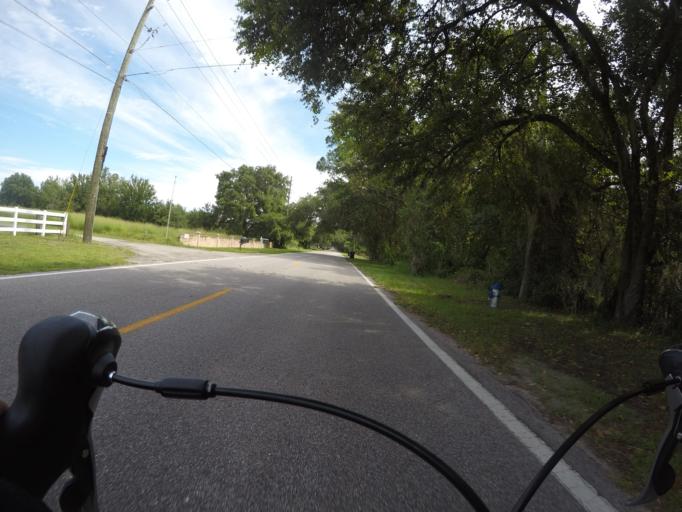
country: US
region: Florida
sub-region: Osceola County
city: Buenaventura Lakes
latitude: 28.3841
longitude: -81.2279
